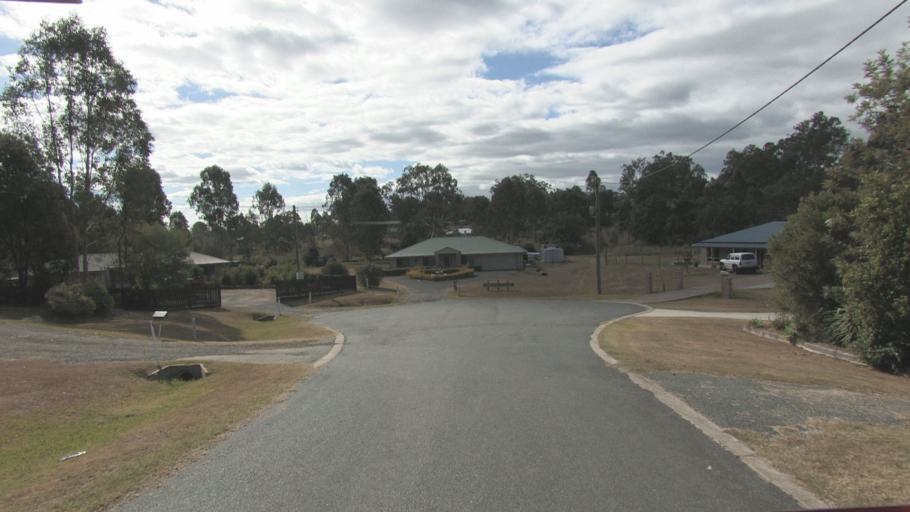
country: AU
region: Queensland
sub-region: Logan
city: Cedar Vale
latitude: -27.8713
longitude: 152.9993
